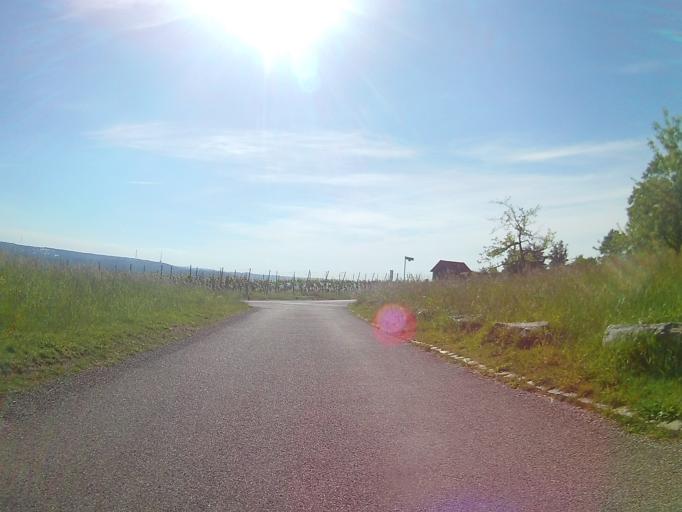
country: DE
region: Baden-Wuerttemberg
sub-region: Regierungsbezirk Stuttgart
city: Fellbach
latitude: 48.7839
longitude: 9.2881
